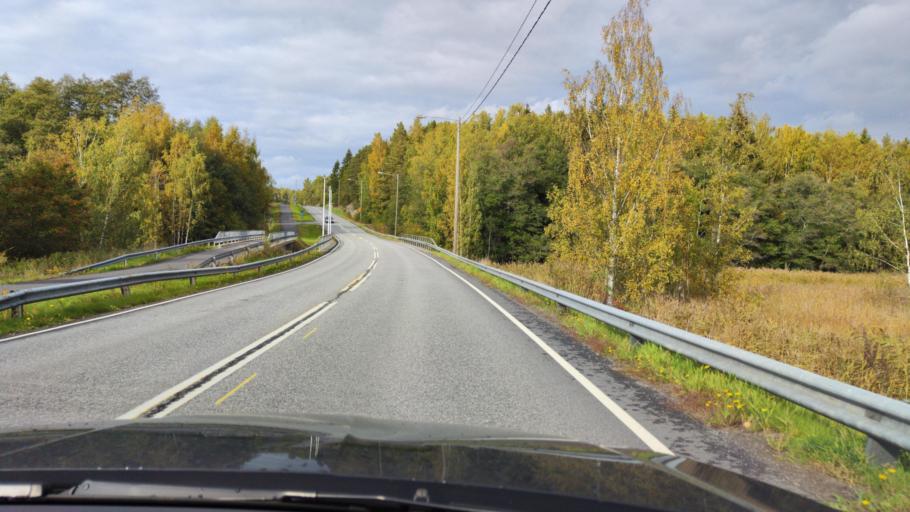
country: FI
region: Varsinais-Suomi
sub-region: Turku
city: Raisio
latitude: 60.3645
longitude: 22.1783
